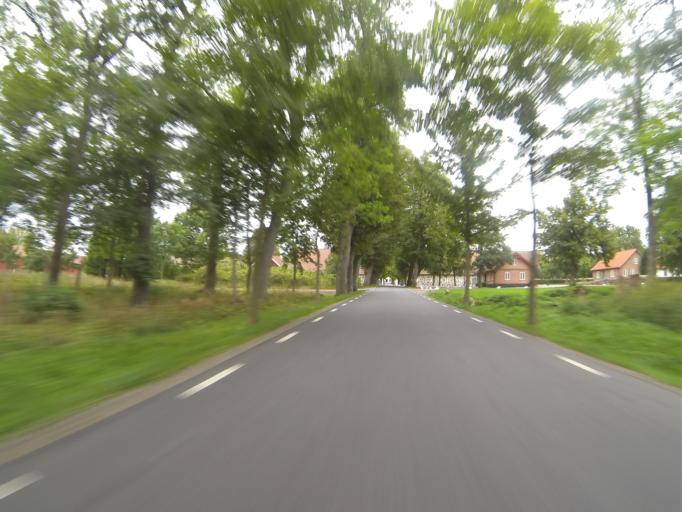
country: SE
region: Skane
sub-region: Lunds Kommun
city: Genarp
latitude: 55.6246
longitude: 13.4063
